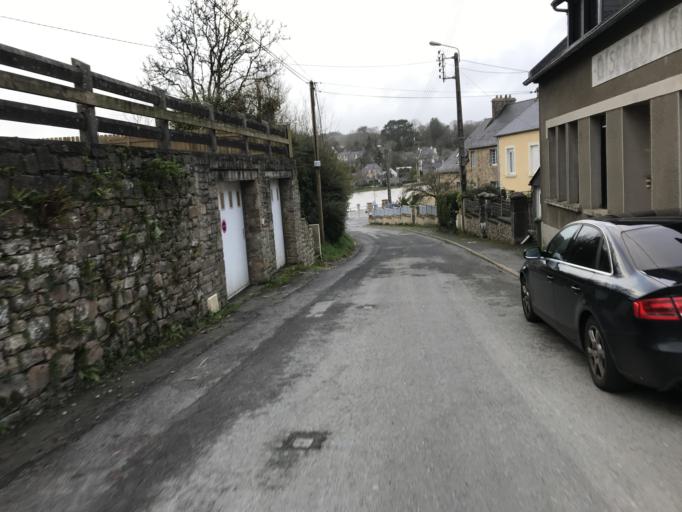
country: FR
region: Brittany
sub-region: Departement du Finistere
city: Daoulas
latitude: 48.3582
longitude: -4.2607
